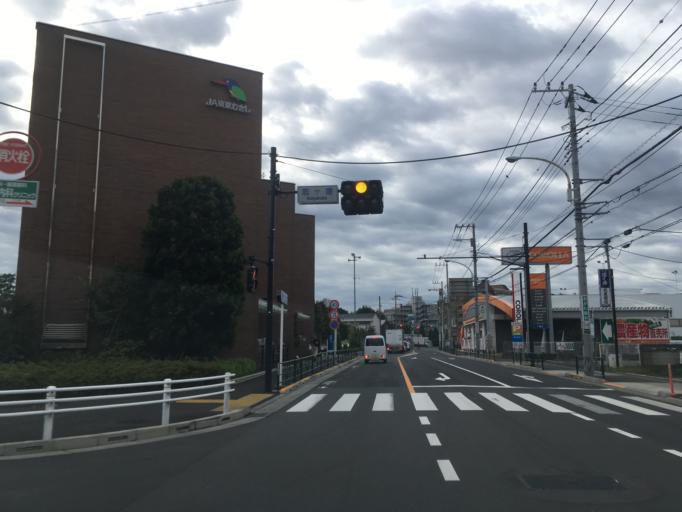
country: JP
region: Tokyo
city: Kokubunji
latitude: 35.7124
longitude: 139.4674
